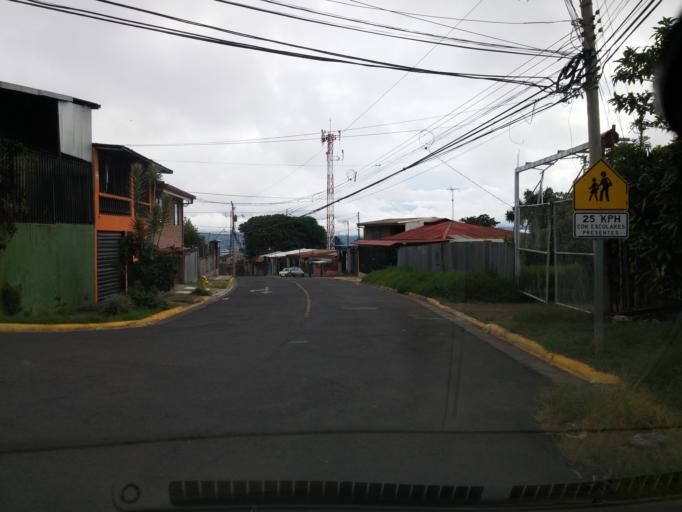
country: CR
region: Heredia
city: San Josecito
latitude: 10.0225
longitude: -84.1043
